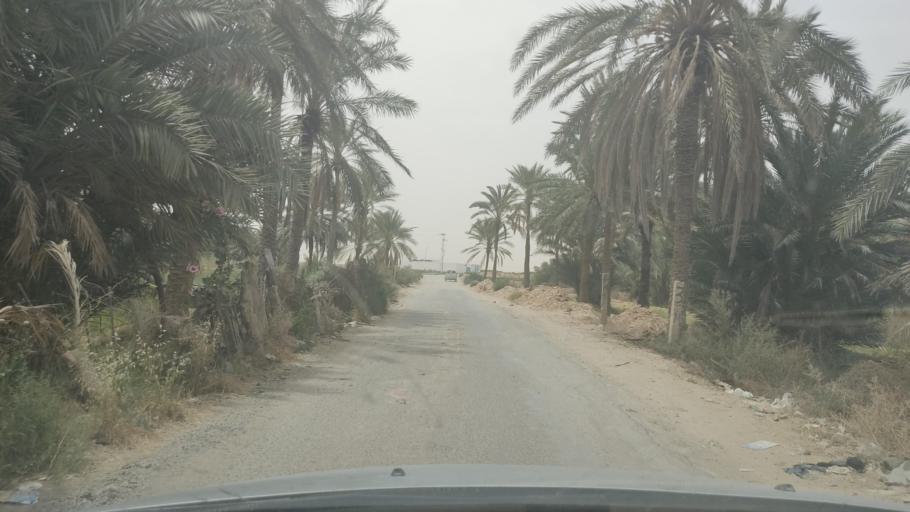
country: TN
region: Gafsa
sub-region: Gafsa Municipality
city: Gafsa
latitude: 34.3268
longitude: 8.9517
